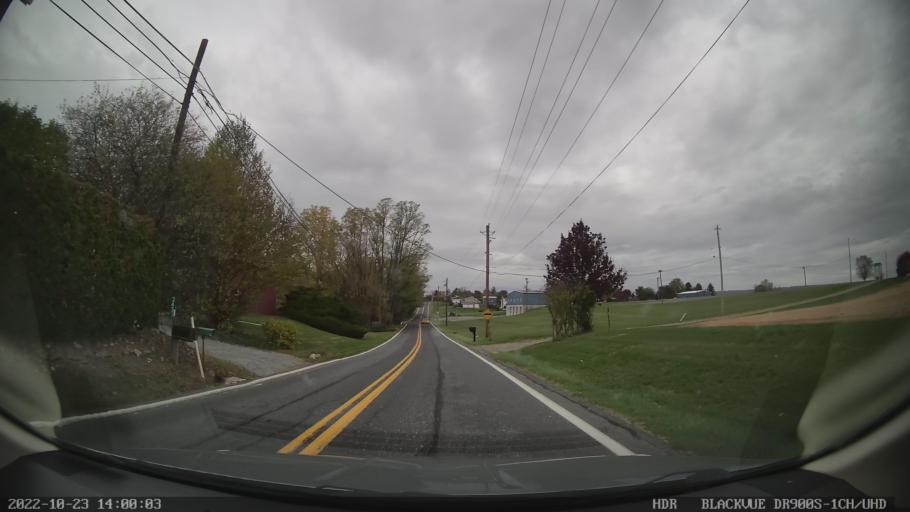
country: US
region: Pennsylvania
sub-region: Northampton County
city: Northampton
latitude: 40.7122
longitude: -75.4809
